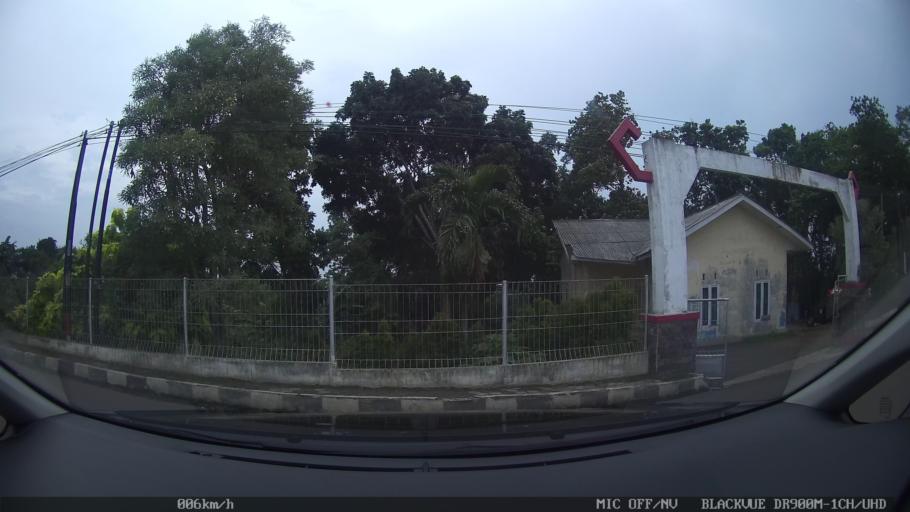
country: ID
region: Lampung
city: Kedaton
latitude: -5.3909
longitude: 105.2163
